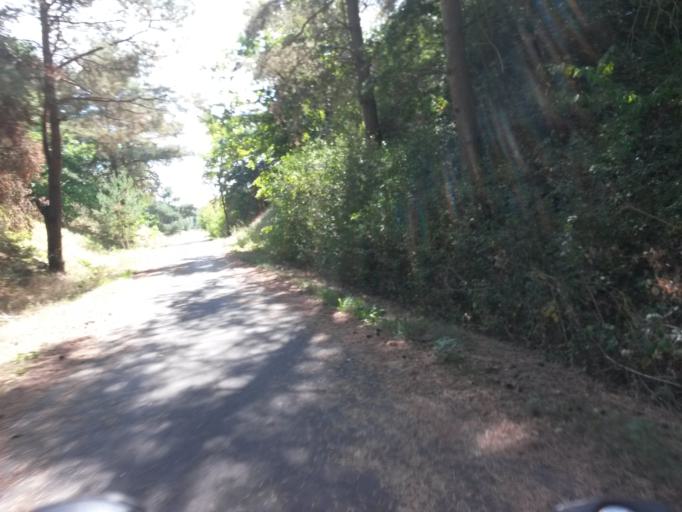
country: DE
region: Brandenburg
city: Templin
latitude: 53.1514
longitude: 13.5317
